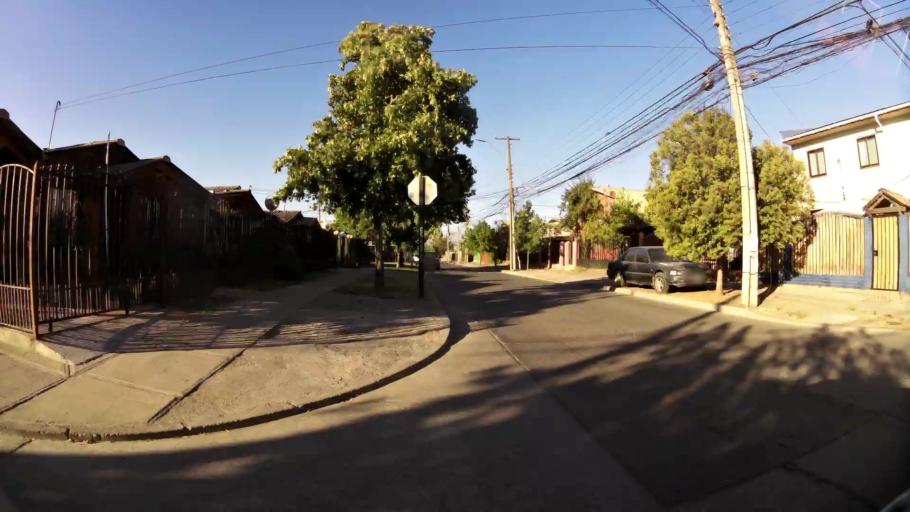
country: CL
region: O'Higgins
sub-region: Provincia de Cachapoal
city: Rancagua
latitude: -34.1765
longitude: -70.7634
